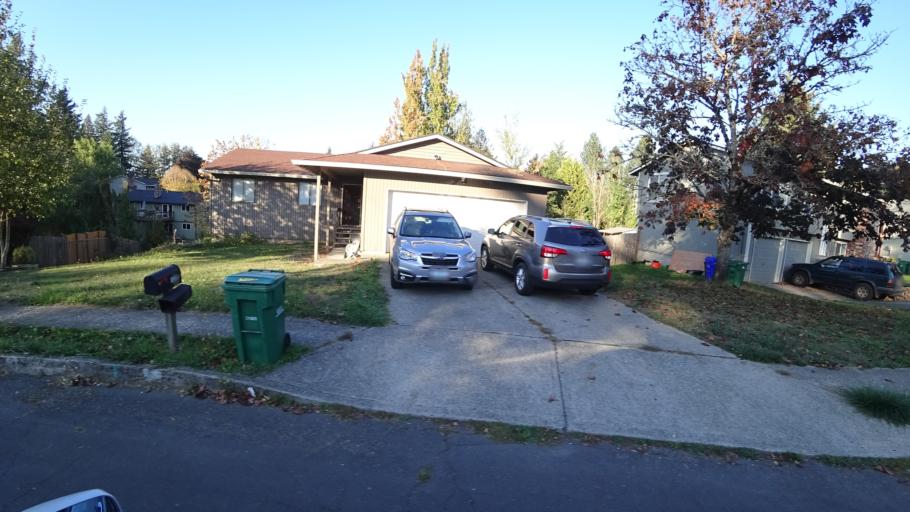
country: US
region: Oregon
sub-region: Multnomah County
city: Gresham
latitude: 45.4863
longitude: -122.4518
